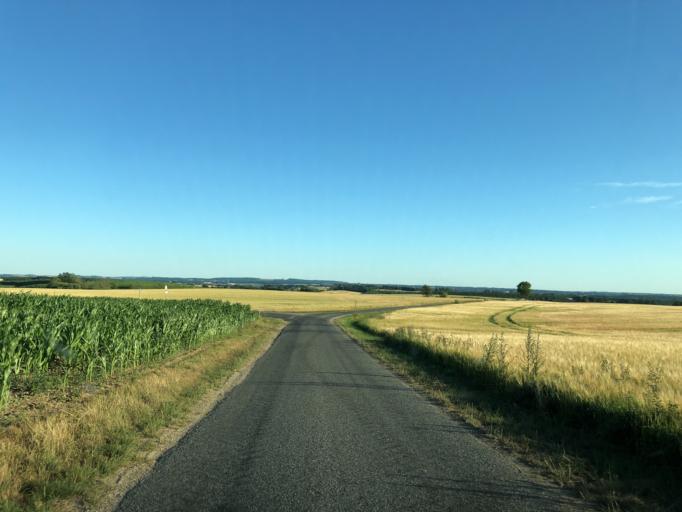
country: DK
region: Central Jutland
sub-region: Horsens Kommune
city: Horsens
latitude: 55.9116
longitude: 9.8753
